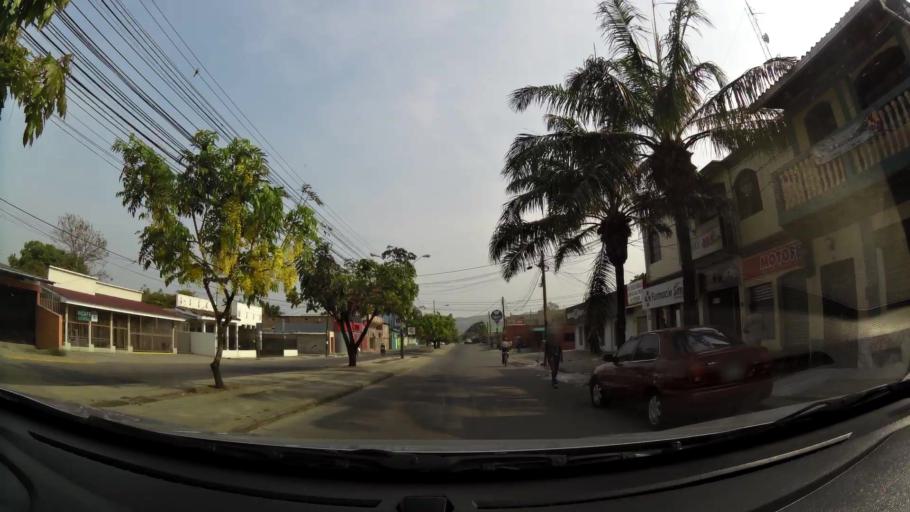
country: HN
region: Comayagua
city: Comayagua
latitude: 14.4574
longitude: -87.6443
